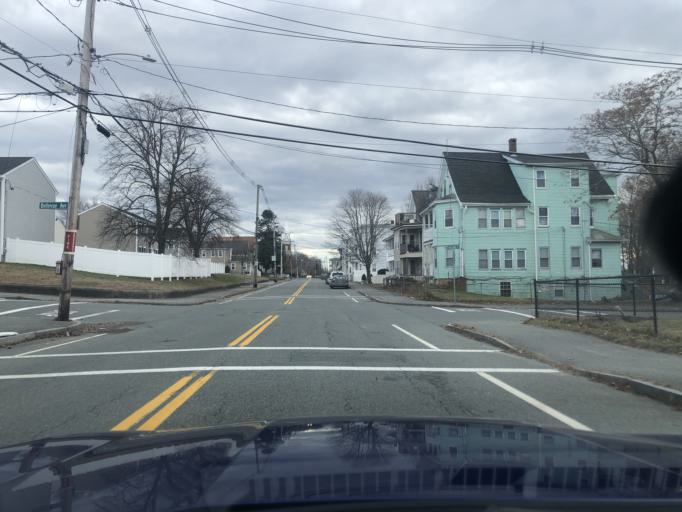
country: US
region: Massachusetts
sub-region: Plymouth County
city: Brockton
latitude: 42.1043
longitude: -71.0133
